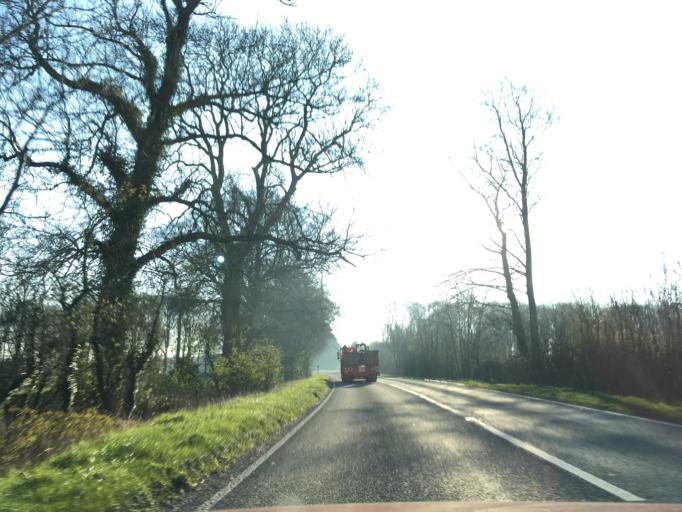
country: GB
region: England
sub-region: Oxfordshire
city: Burford
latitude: 51.8070
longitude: -1.6960
